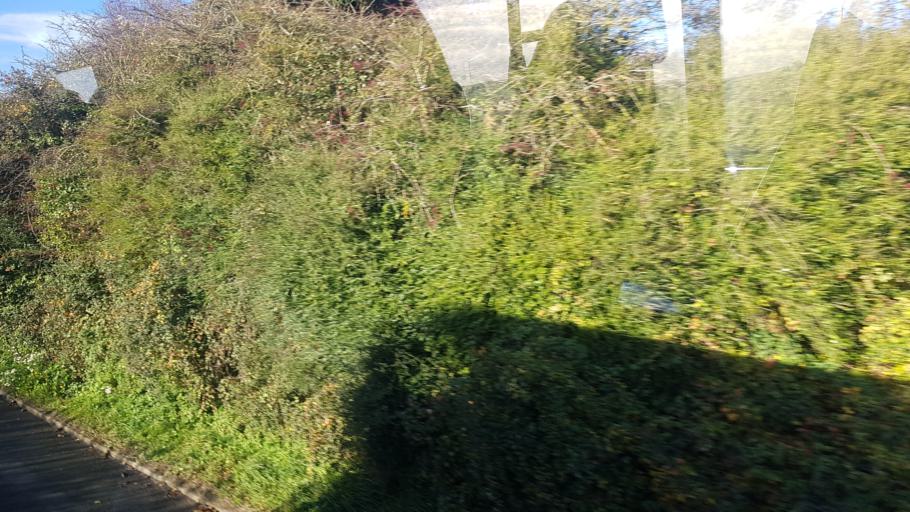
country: GB
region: England
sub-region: Isle of Wight
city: Newport
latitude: 50.6846
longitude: -1.3259
